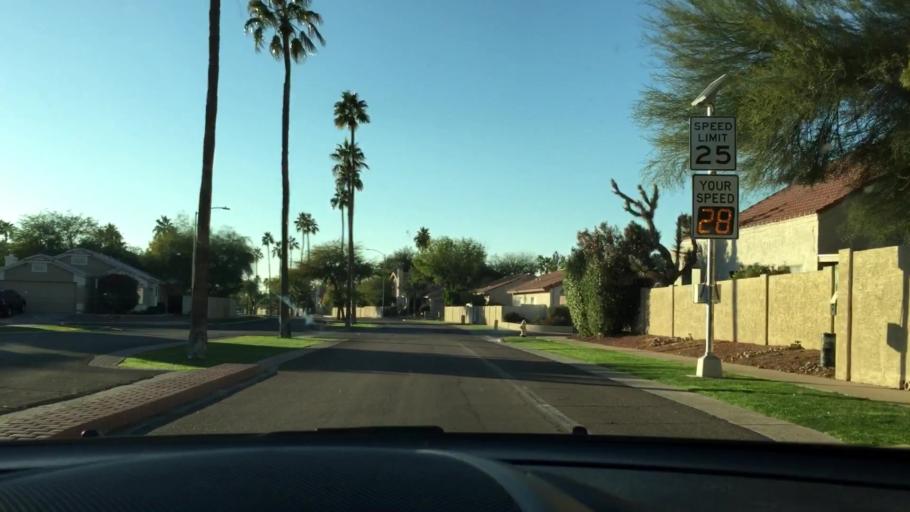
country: US
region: Arizona
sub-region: Maricopa County
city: Sun City
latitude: 33.6601
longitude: -112.2222
